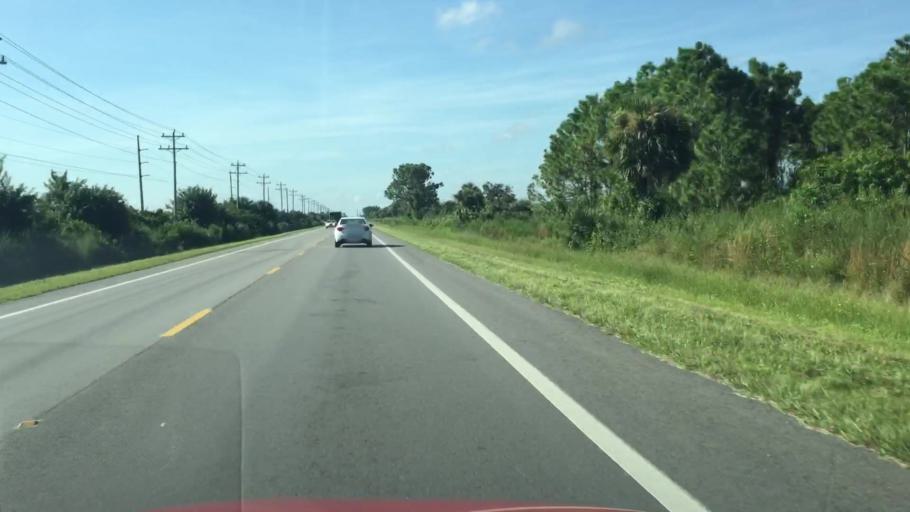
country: US
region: Florida
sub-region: Collier County
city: Immokalee
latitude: 26.3918
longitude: -81.4171
